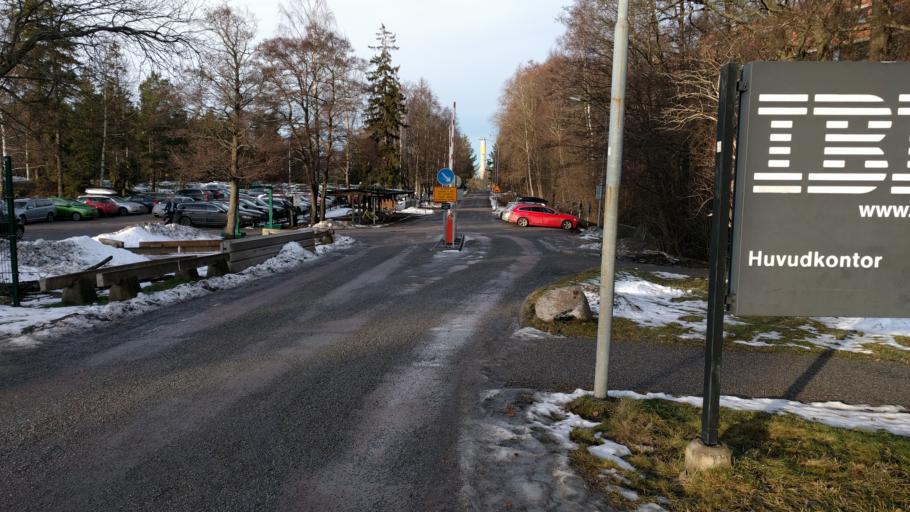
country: SE
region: Stockholm
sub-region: Stockholms Kommun
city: Kista
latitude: 59.4101
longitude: 17.9382
